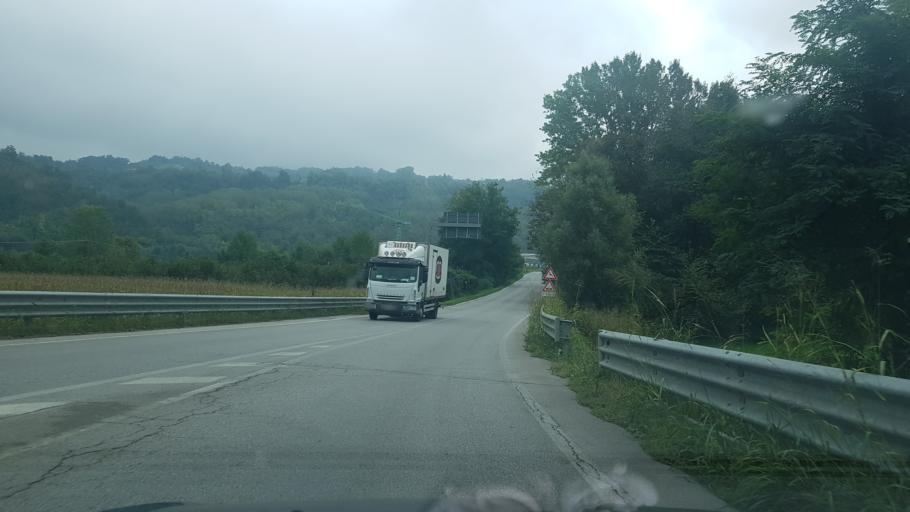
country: IT
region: Piedmont
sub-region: Provincia di Cuneo
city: Bastia Mondovi
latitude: 44.4512
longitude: 7.8931
